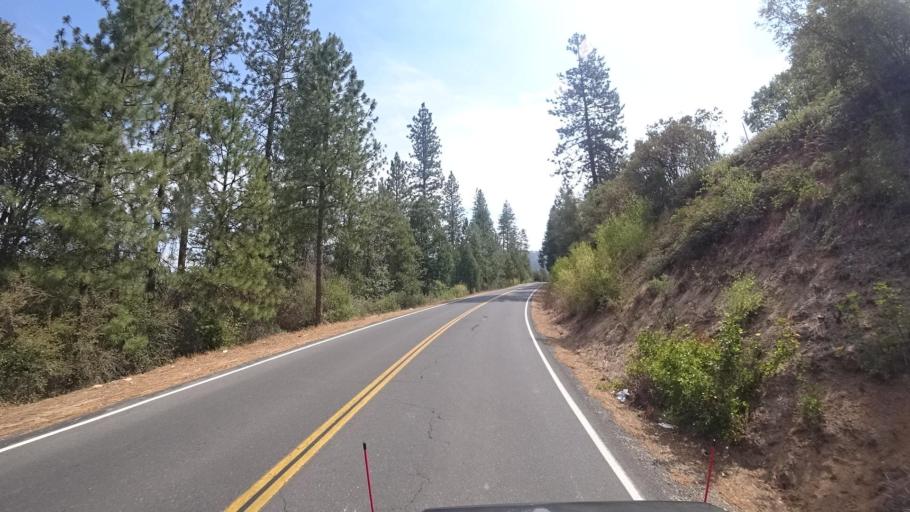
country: US
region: California
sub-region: Mariposa County
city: Midpines
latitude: 37.5137
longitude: -119.8412
